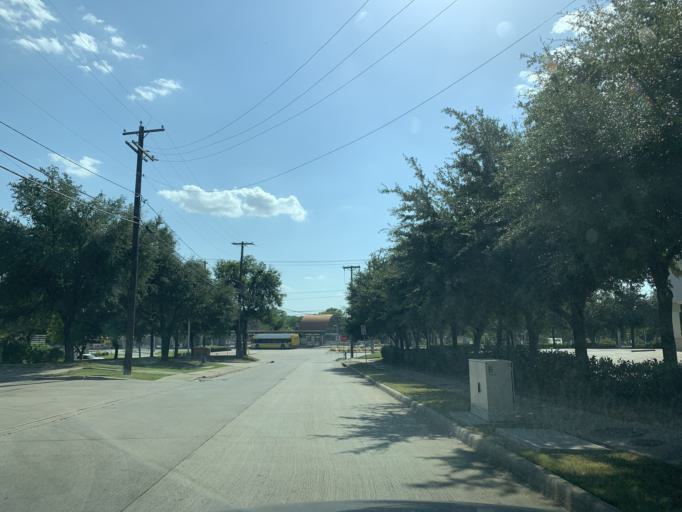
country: US
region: Texas
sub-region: Dallas County
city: Hutchins
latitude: 32.6844
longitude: -96.7875
